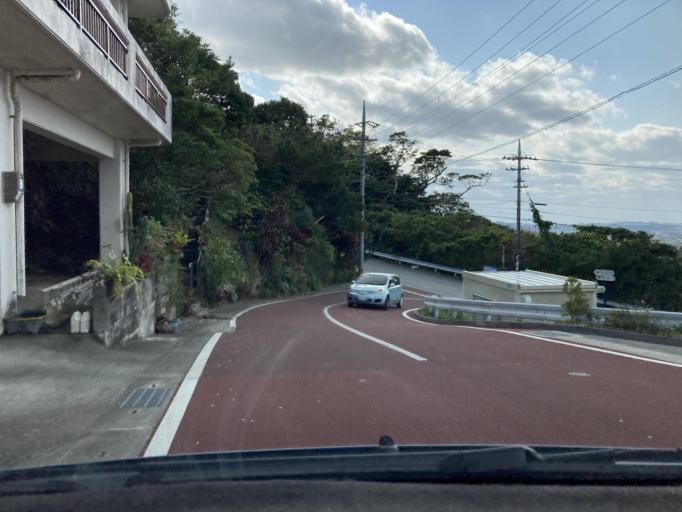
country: JP
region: Okinawa
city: Tomigusuku
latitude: 26.1847
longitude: 127.7593
